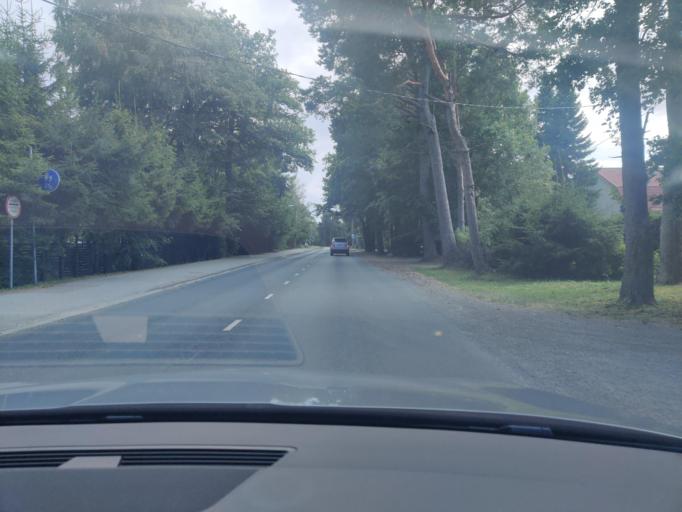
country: EE
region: Harju
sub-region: Harku vald
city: Tabasalu
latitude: 59.4370
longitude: 24.6003
